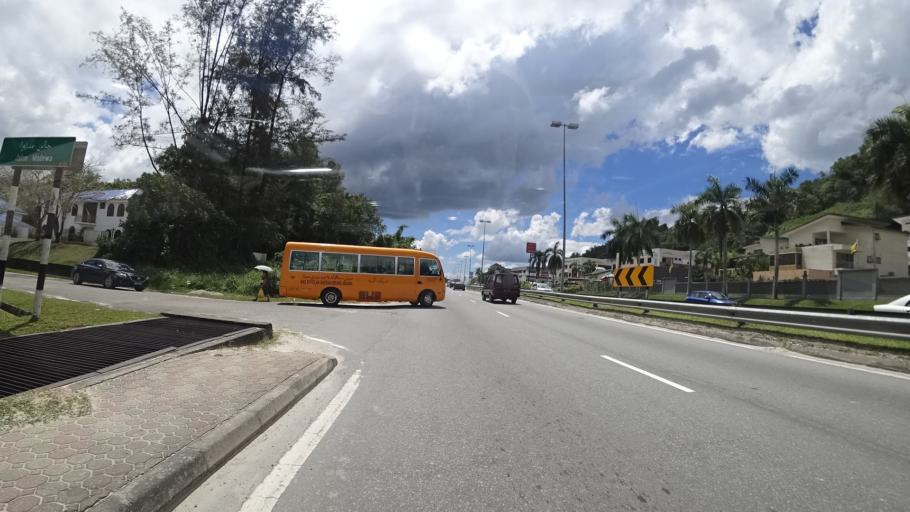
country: BN
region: Brunei and Muara
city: Bandar Seri Begawan
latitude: 4.8605
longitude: 114.8972
